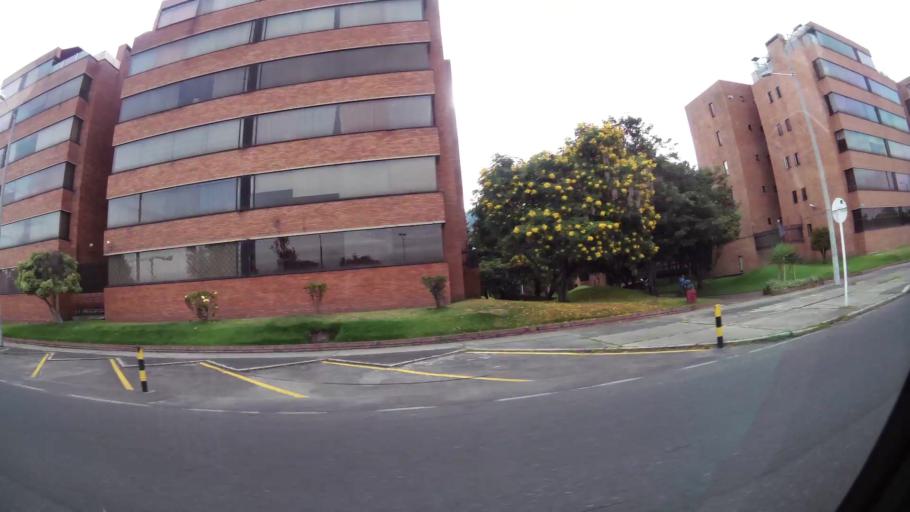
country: CO
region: Bogota D.C.
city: Barrio San Luis
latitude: 4.7024
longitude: -74.0396
